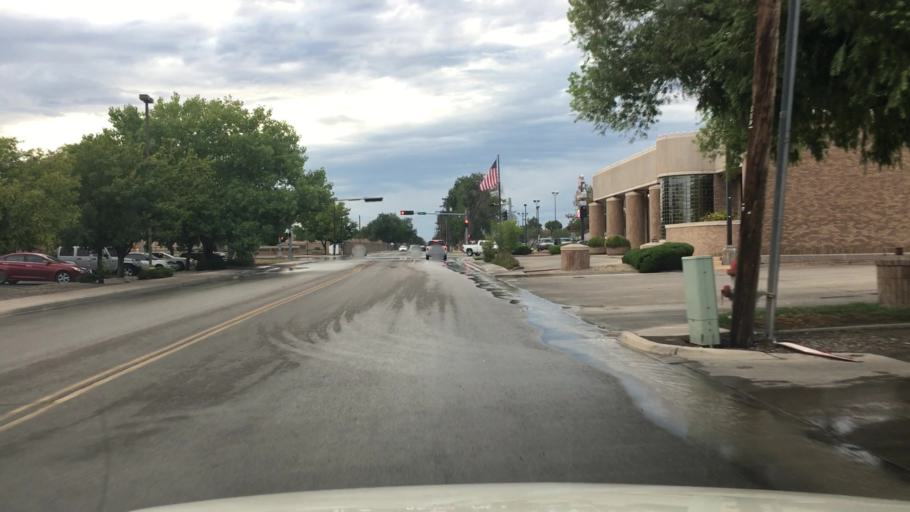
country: US
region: New Mexico
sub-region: Chaves County
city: Roswell
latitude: 33.4160
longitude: -104.5219
